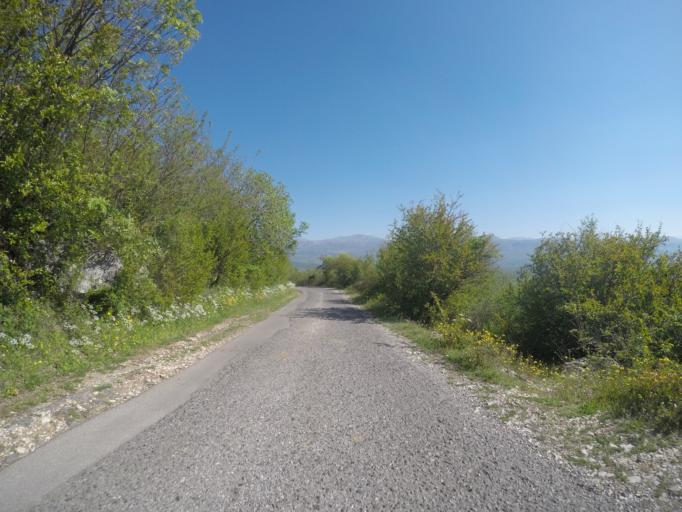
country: ME
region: Danilovgrad
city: Danilovgrad
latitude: 42.5142
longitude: 19.0979
